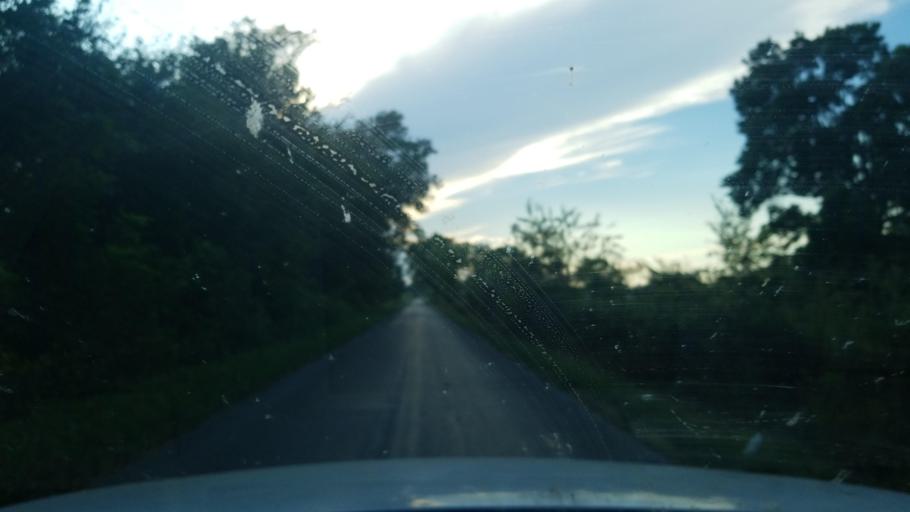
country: US
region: Illinois
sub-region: Saline County
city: Carrier Mills
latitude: 37.7938
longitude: -88.6557
